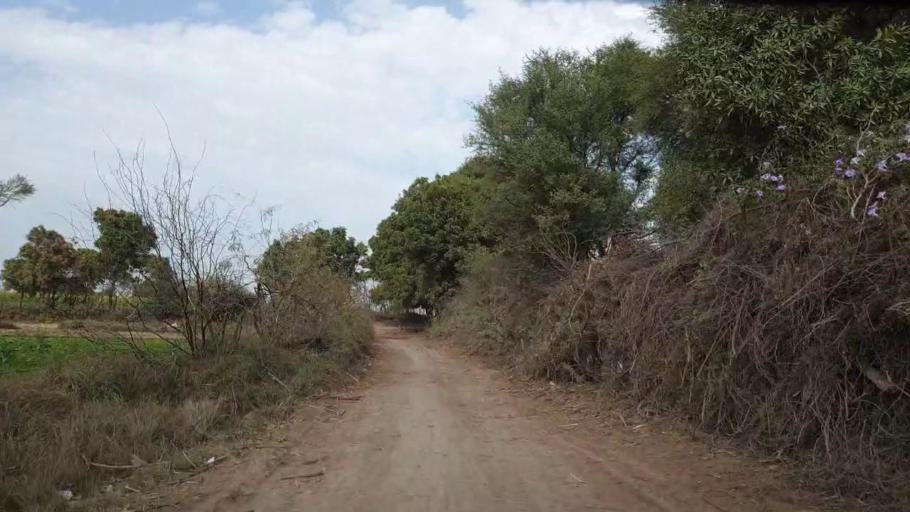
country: PK
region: Sindh
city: Matiari
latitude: 25.5581
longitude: 68.5748
